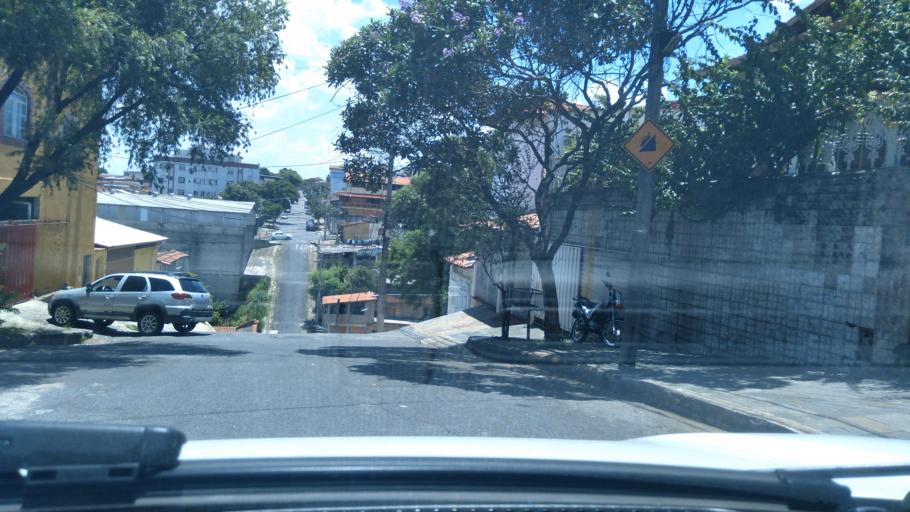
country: BR
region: Minas Gerais
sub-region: Contagem
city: Contagem
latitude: -19.9294
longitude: -43.9984
